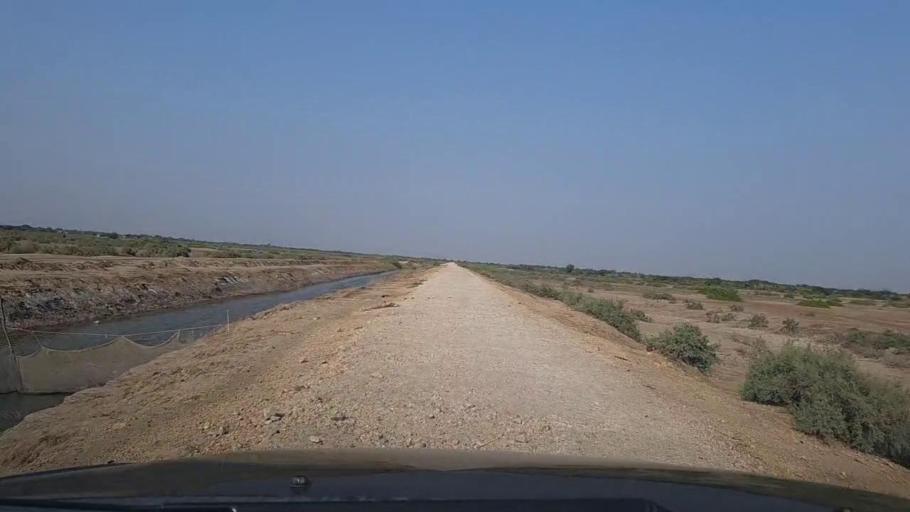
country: PK
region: Sindh
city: Mirpur Sakro
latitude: 24.6421
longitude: 67.7518
